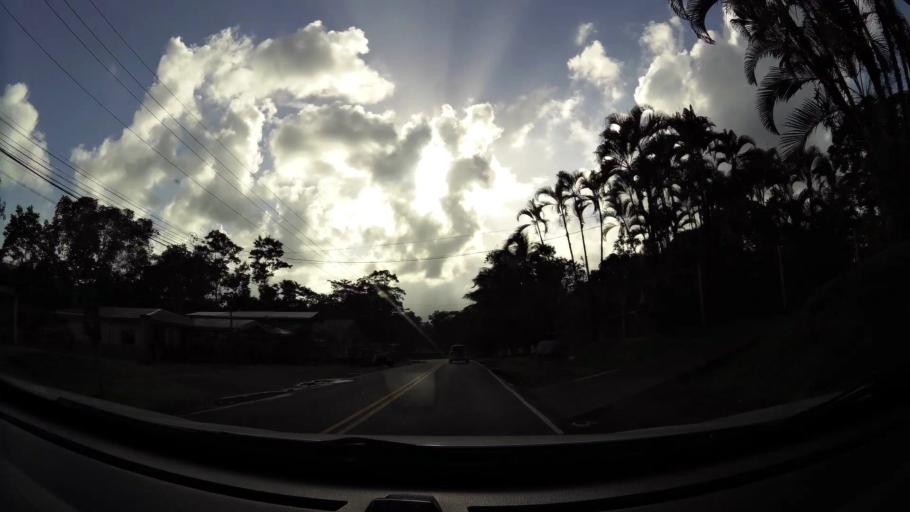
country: CR
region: Limon
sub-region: Canton de Siquirres
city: Siquirres
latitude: 10.0936
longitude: -83.5385
